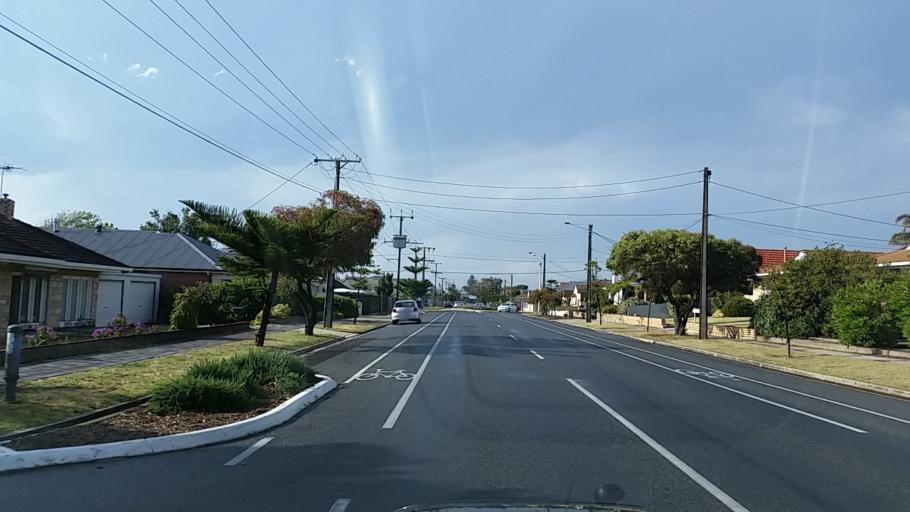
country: AU
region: South Australia
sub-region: Charles Sturt
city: Henley Beach
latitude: -34.9116
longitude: 138.4966
